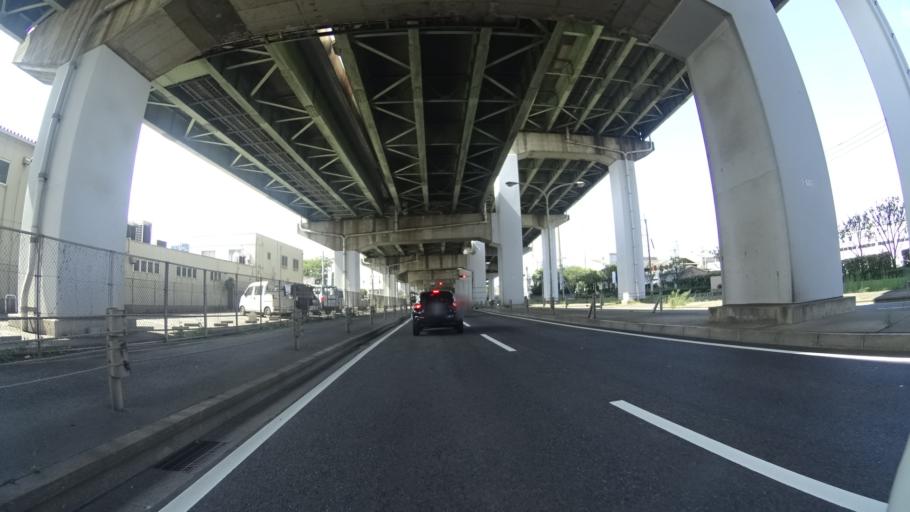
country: JP
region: Fukuoka
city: Kitakyushu
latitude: 33.8916
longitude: 130.8673
